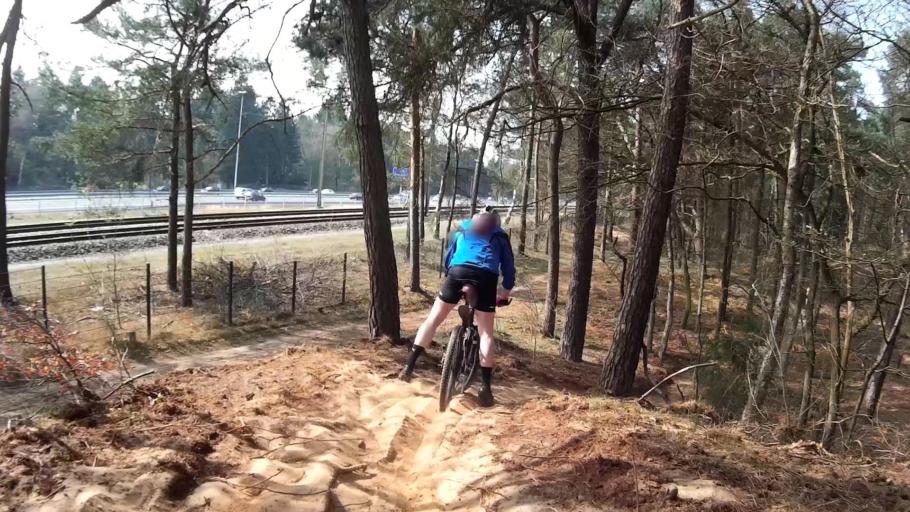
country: NL
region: Utrecht
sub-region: Gemeente Utrechtse Heuvelrug
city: Driebergen-Rijsenburg
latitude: 52.0661
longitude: 5.3121
